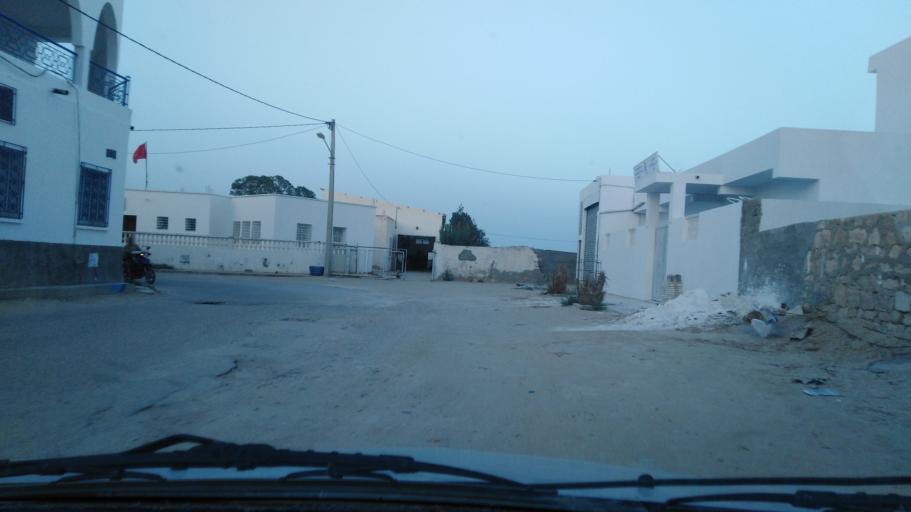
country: TN
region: Qabis
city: Gabes
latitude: 33.9562
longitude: 9.9984
